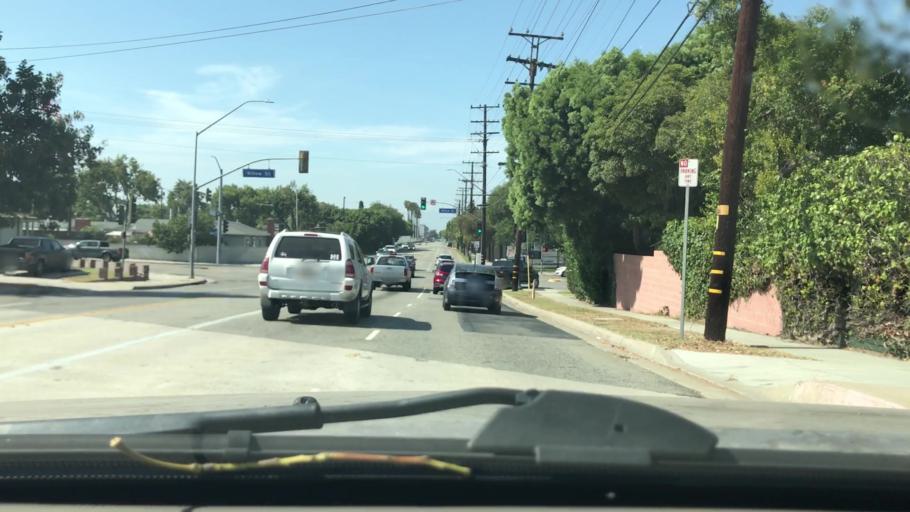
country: US
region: California
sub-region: Orange County
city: Rossmoor
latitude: 33.8026
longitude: -118.1079
